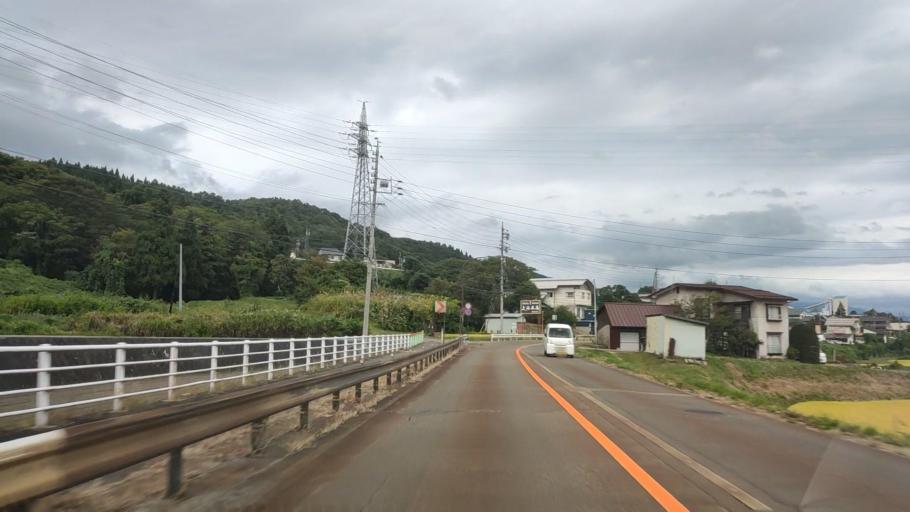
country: JP
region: Nagano
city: Iiyama
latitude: 36.8185
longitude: 138.3486
